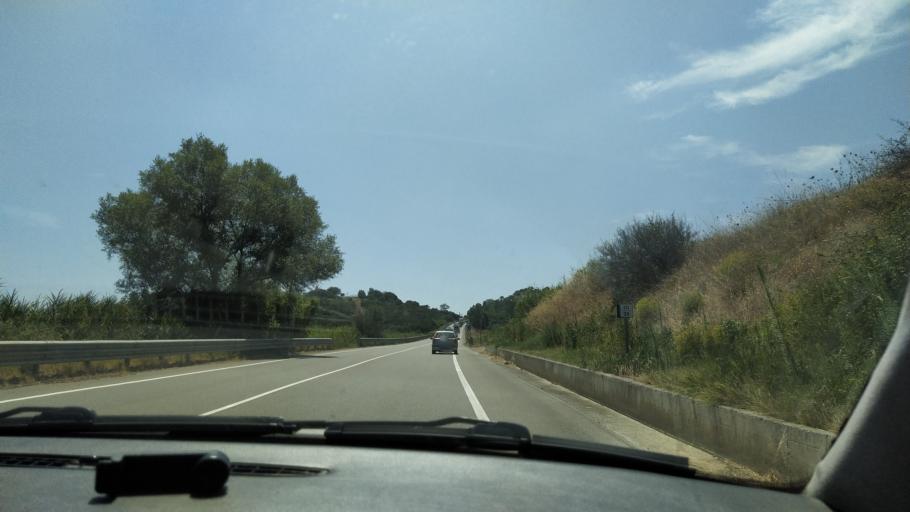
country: IT
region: Apulia
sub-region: Provincia di Taranto
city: Marina di Ginosa
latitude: 40.4309
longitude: 16.7934
